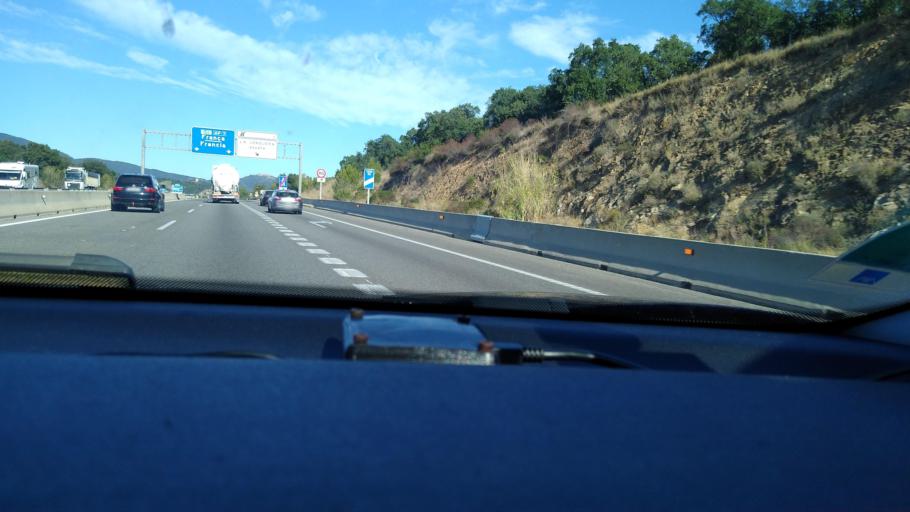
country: ES
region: Catalonia
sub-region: Provincia de Girona
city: la Jonquera
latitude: 42.3966
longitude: 2.8777
